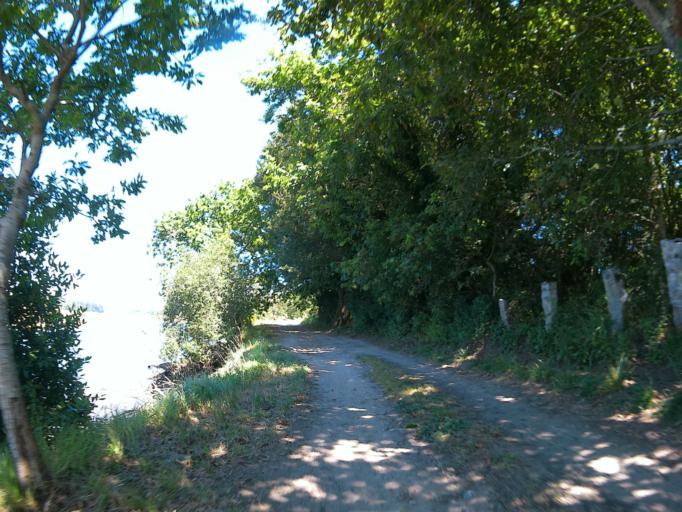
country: PT
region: Viana do Castelo
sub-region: Viana do Castelo
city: Darque
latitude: 41.7000
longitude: -8.7385
